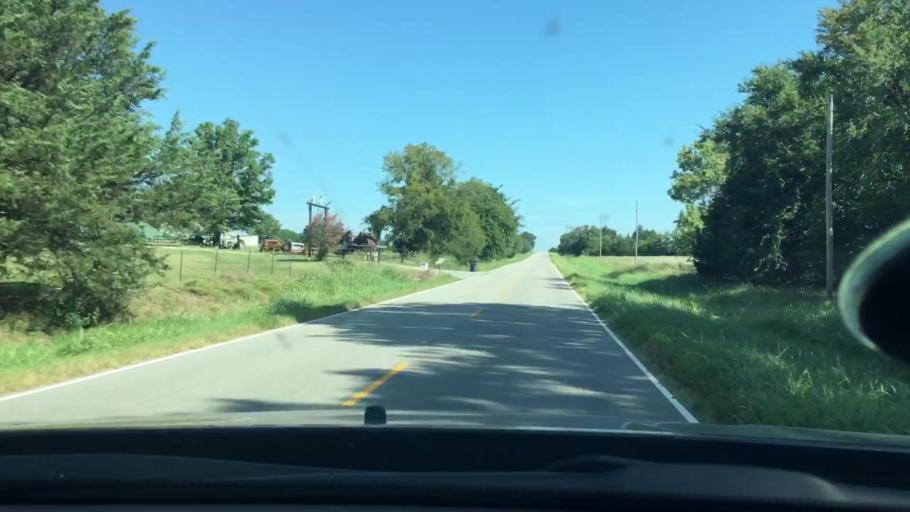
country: US
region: Oklahoma
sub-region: Johnston County
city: Tishomingo
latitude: 34.2933
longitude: -96.5488
